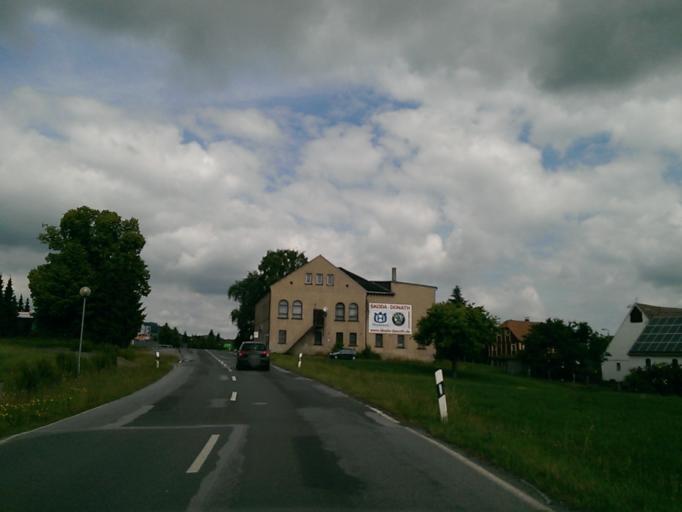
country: DE
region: Saxony
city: Mittelherwigsdorf
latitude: 50.9418
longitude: 14.7436
